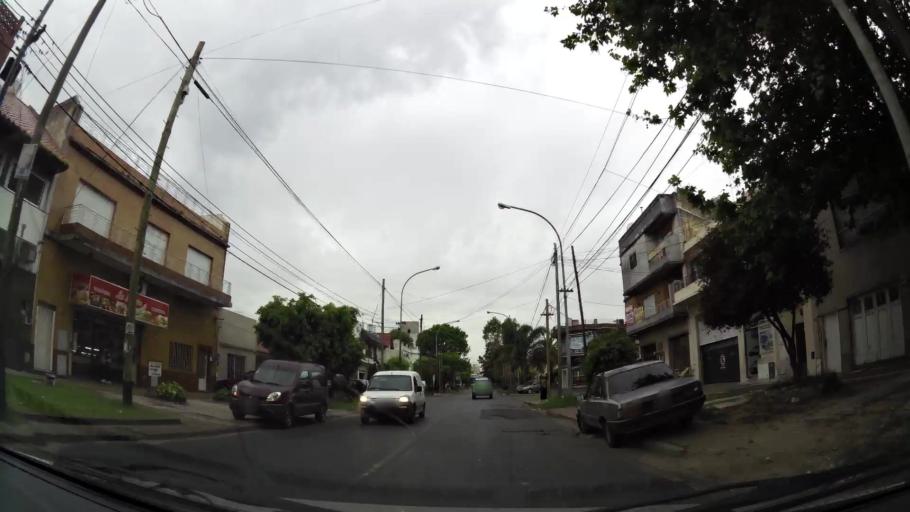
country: AR
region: Buenos Aires
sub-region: Partido de Lanus
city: Lanus
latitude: -34.7002
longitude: -58.4031
